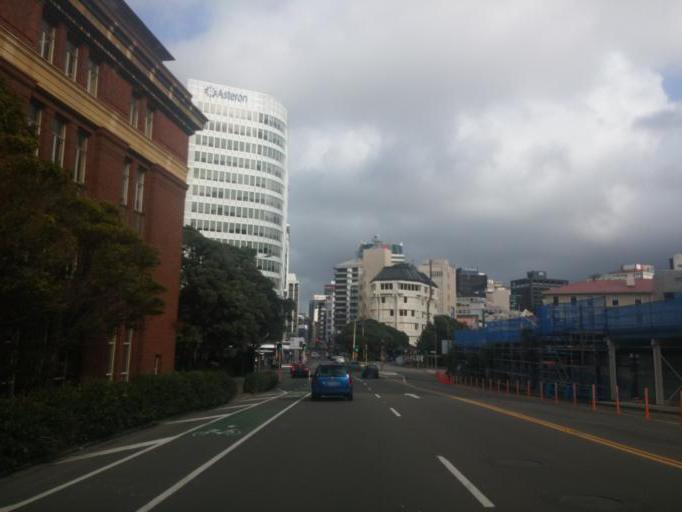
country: NZ
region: Wellington
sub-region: Wellington City
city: Wellington
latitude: -41.2788
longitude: 174.7798
